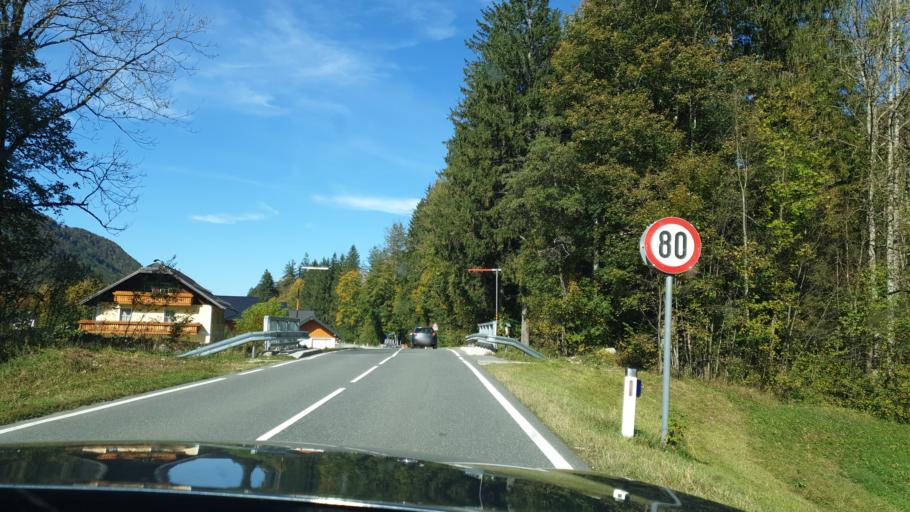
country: AT
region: Salzburg
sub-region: Politischer Bezirk Salzburg-Umgebung
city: Hintersee
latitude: 47.7350
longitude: 13.2645
